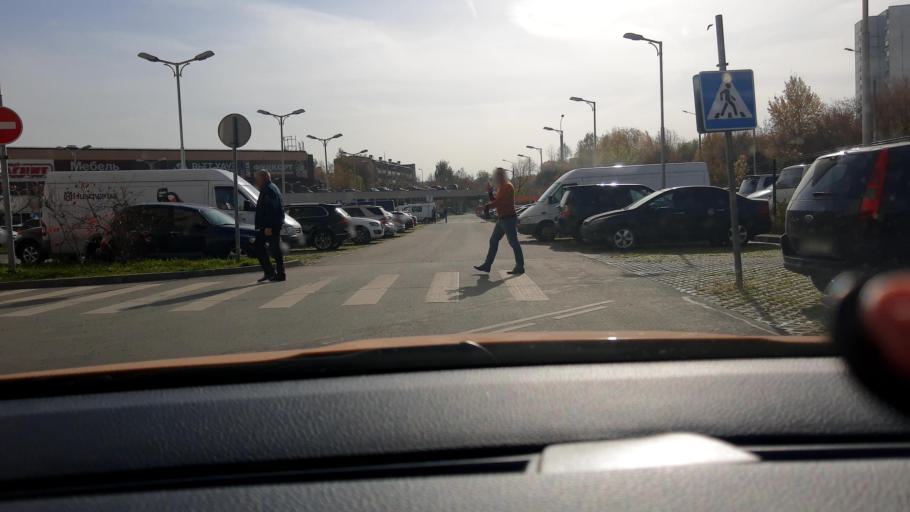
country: RU
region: Moscow
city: Babushkin
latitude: 55.8790
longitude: 37.7284
